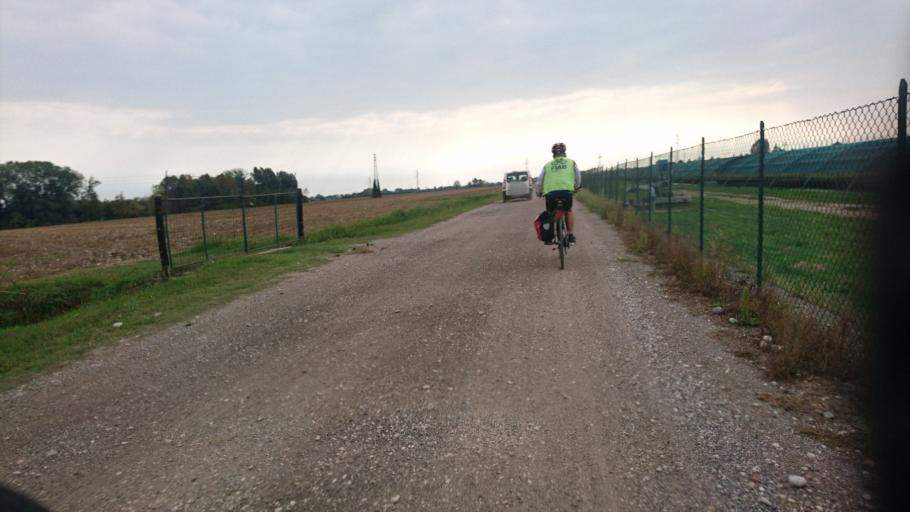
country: IT
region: Veneto
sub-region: Provincia di Verona
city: San Martino Buon Albergo
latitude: 45.4046
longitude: 11.1091
